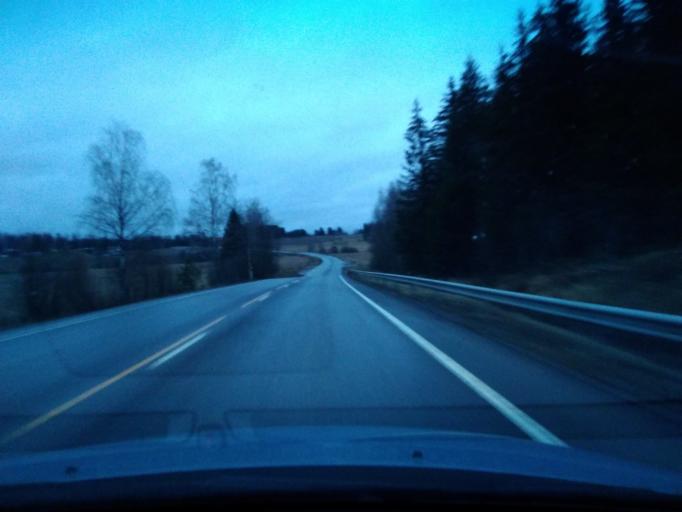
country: FI
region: Uusimaa
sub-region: Porvoo
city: Askola
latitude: 60.4397
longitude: 25.5790
